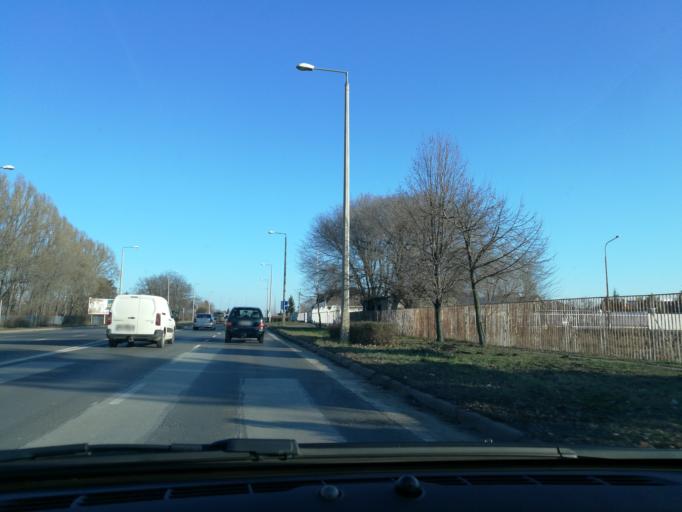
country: HU
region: Szabolcs-Szatmar-Bereg
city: Nyiregyhaza
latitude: 47.9518
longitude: 21.7467
